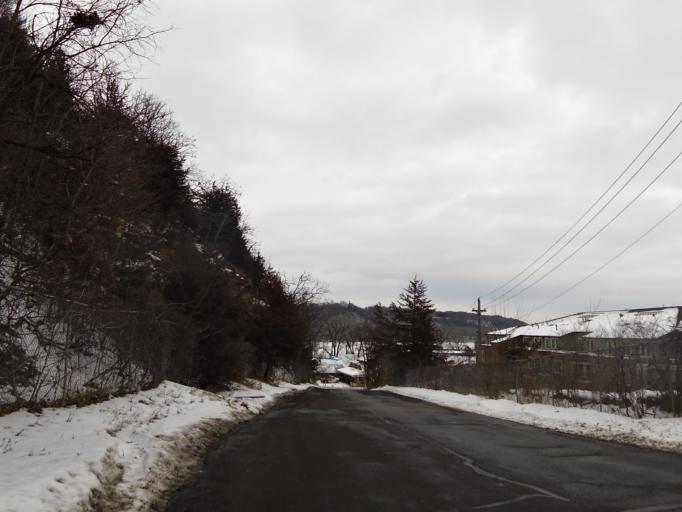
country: US
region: Minnesota
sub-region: Washington County
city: Stillwater
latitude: 45.0635
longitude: -92.8080
